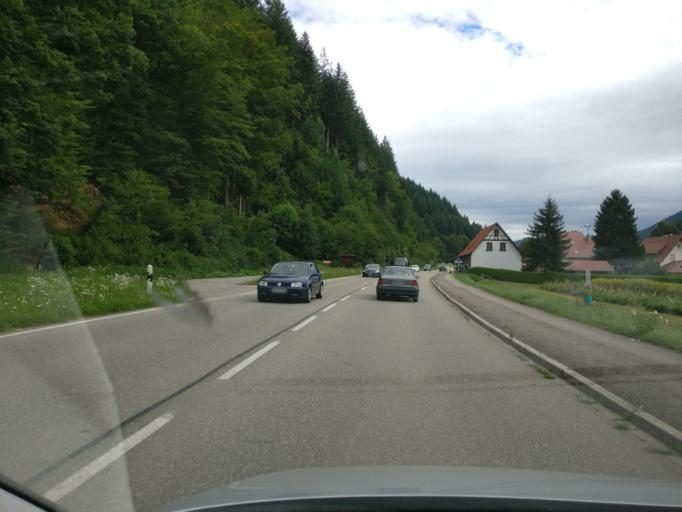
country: DE
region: Baden-Wuerttemberg
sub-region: Freiburg Region
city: Oppenau
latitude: 48.4875
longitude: 8.1496
